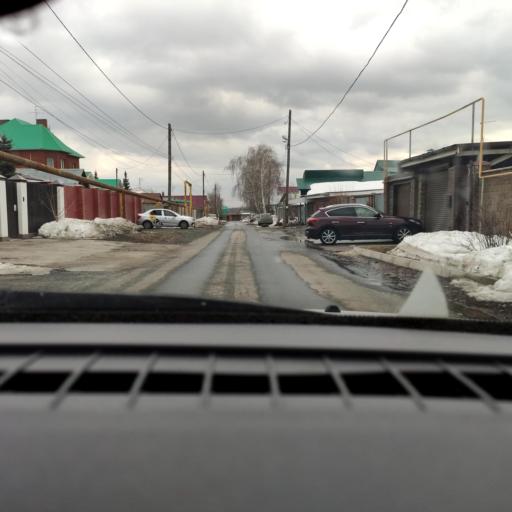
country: RU
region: Samara
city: Petra-Dubrava
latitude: 53.2953
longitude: 50.2791
